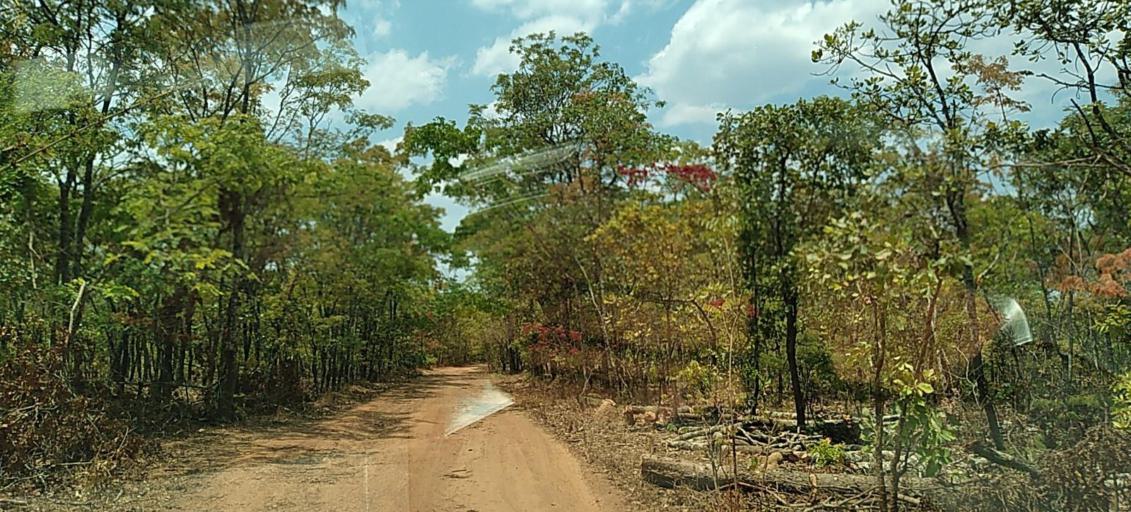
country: ZM
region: Copperbelt
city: Chililabombwe
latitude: -12.5125
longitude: 27.6293
